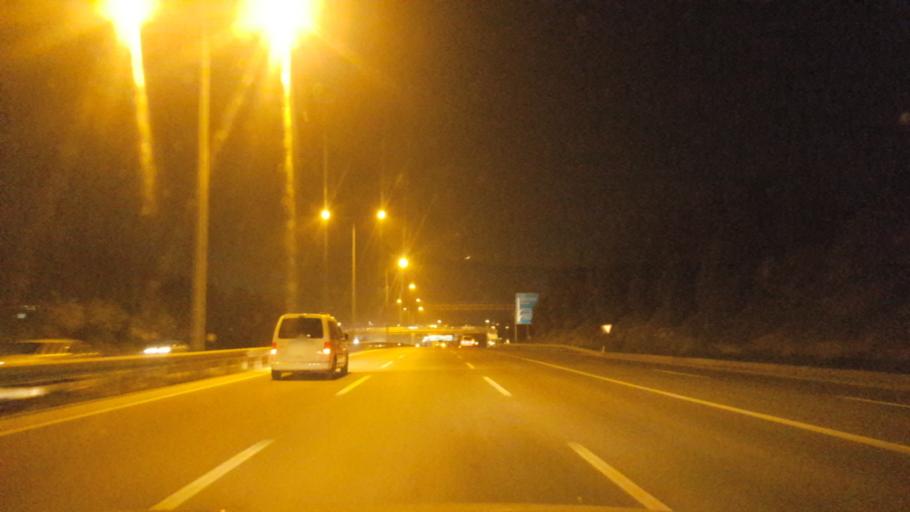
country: TR
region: Kocaeli
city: Gebze
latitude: 40.8016
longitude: 29.4698
